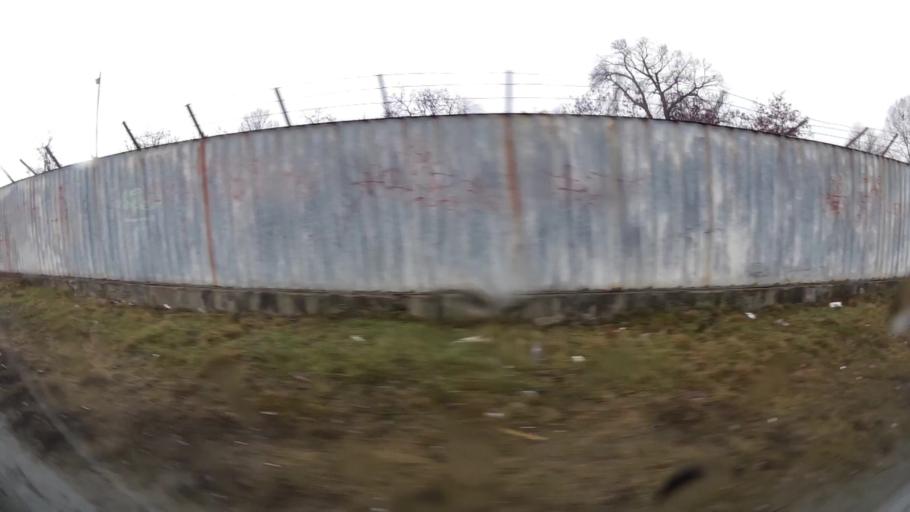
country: BG
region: Sofia-Capital
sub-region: Stolichna Obshtina
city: Sofia
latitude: 42.6571
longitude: 23.4271
